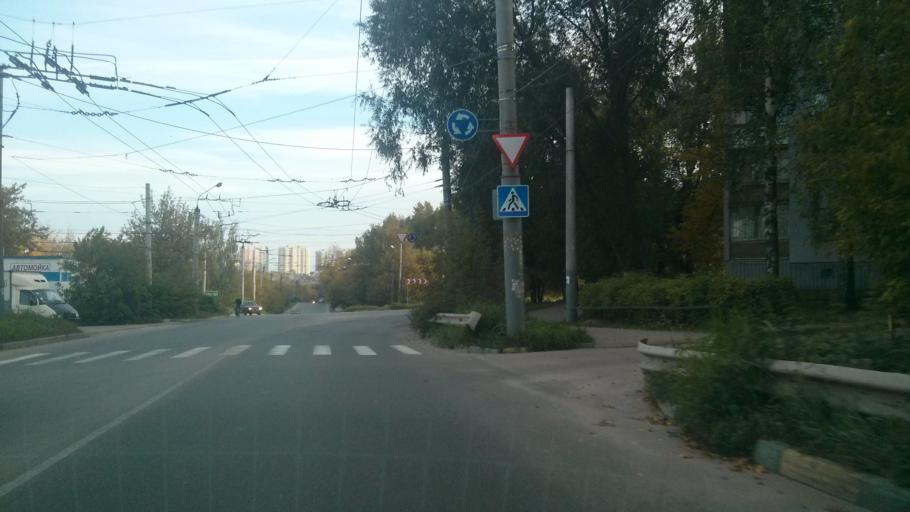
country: RU
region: Nizjnij Novgorod
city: Afonino
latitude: 56.2970
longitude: 44.0511
